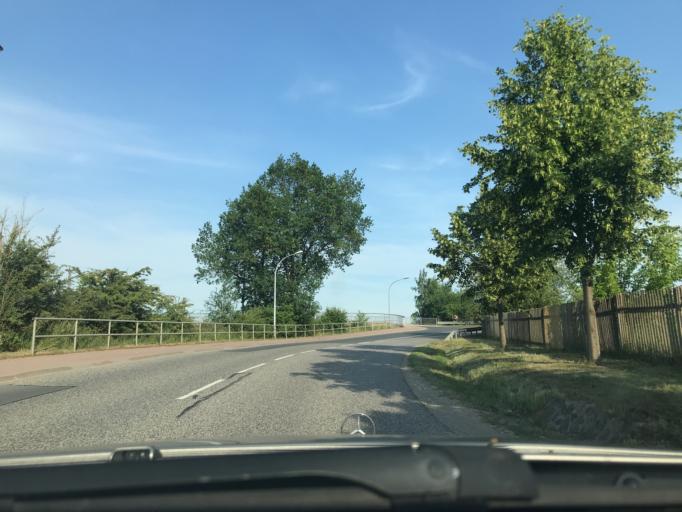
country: DE
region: Thuringia
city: Leinefelde
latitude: 51.3863
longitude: 10.3386
